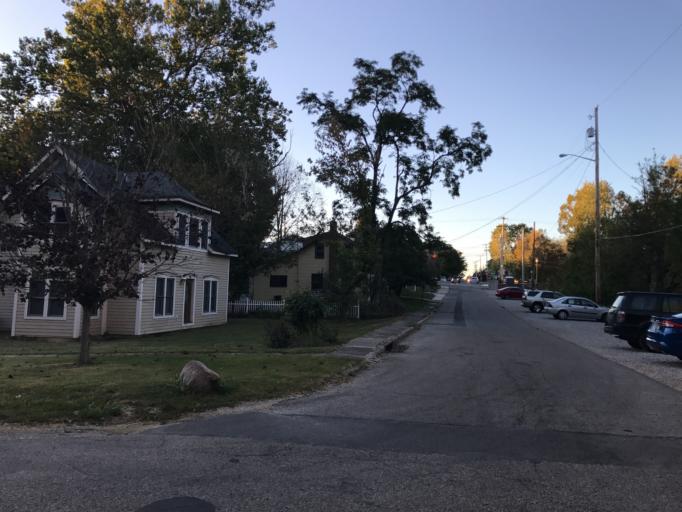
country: US
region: Ohio
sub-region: Delaware County
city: Sunbury
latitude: 40.2143
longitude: -82.8790
